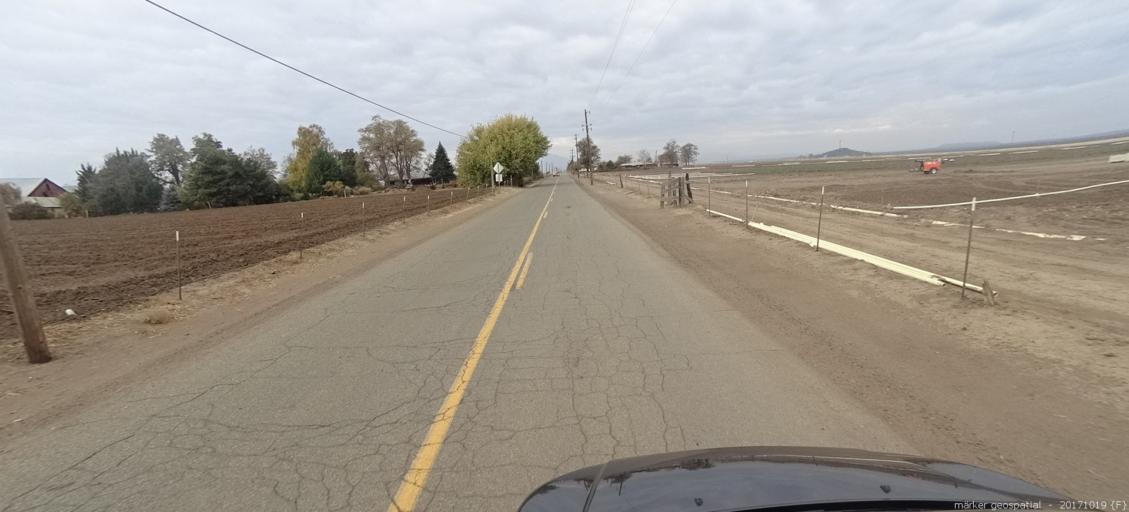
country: US
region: California
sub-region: Shasta County
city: Burney
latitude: 41.0806
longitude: -121.3327
